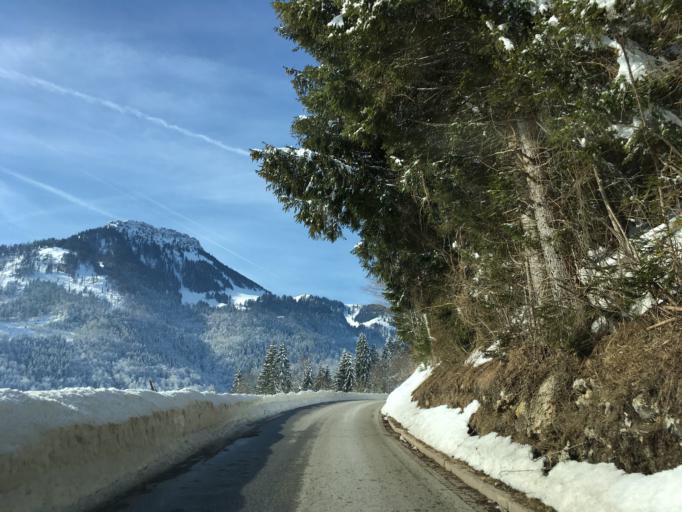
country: DE
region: Bavaria
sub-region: Upper Bavaria
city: Oberaudorf
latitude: 47.6584
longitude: 12.1283
